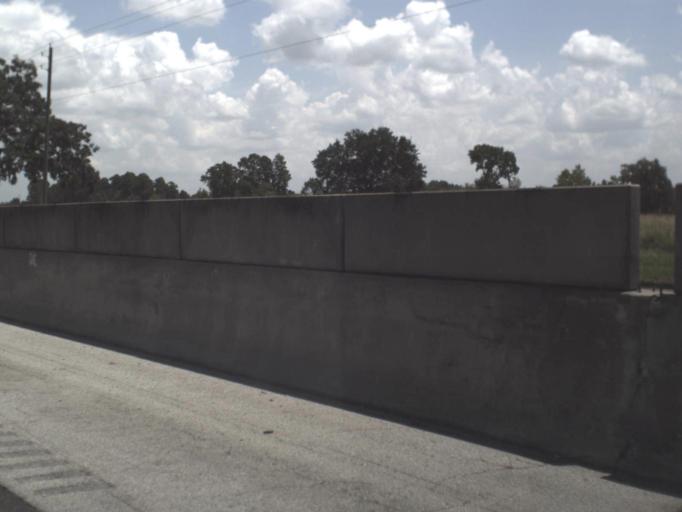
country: US
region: Florida
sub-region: Hillsborough County
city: Plant City
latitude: 28.0367
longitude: -82.0835
